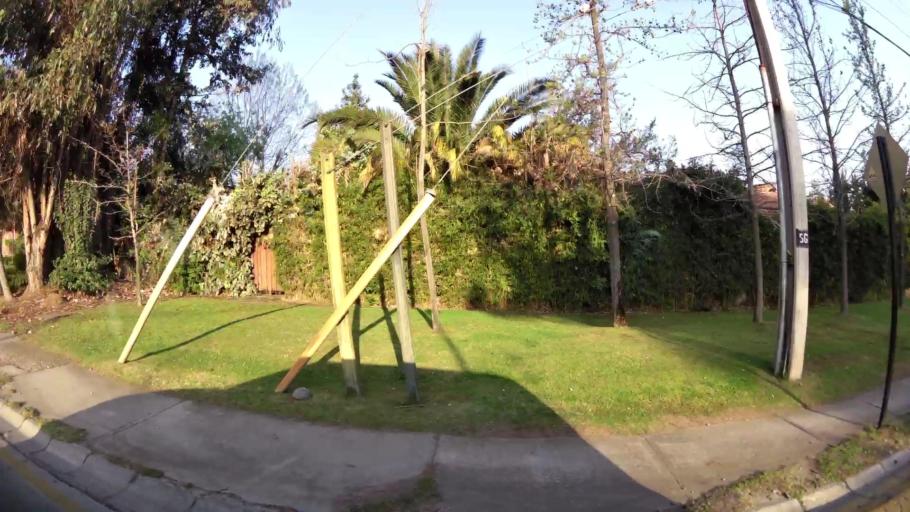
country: CL
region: Santiago Metropolitan
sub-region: Provincia de Santiago
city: Villa Presidente Frei, Nunoa, Santiago, Chile
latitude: -33.3373
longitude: -70.5103
